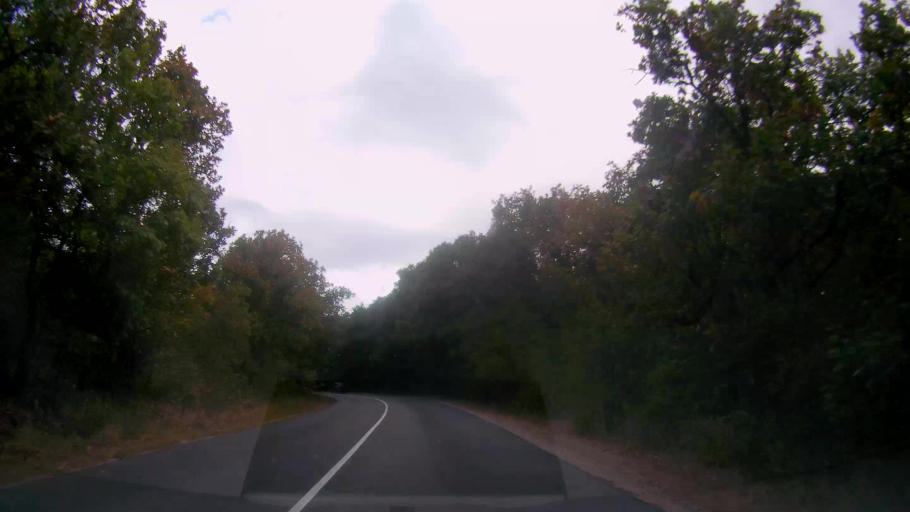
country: BG
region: Burgas
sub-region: Obshtina Primorsko
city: Primorsko
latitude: 42.2945
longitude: 27.7299
